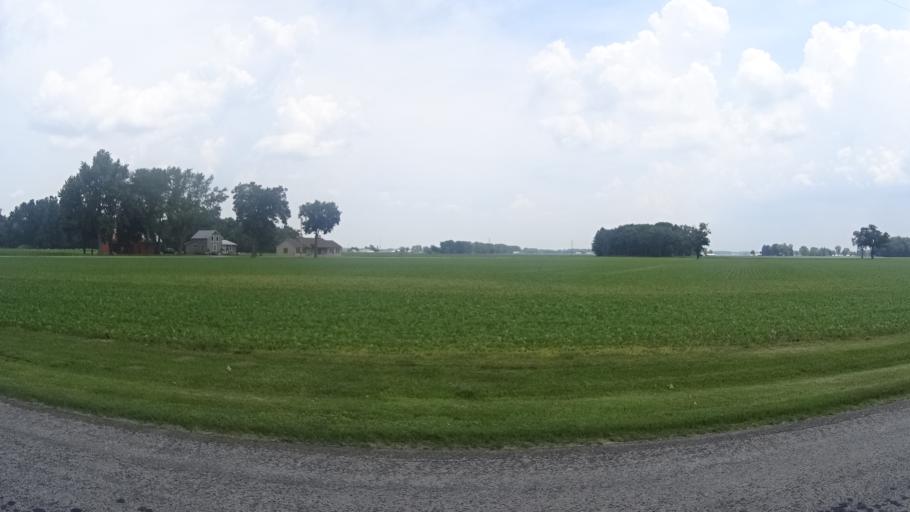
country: US
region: Ohio
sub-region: Erie County
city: Milan
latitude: 41.3153
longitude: -82.6701
